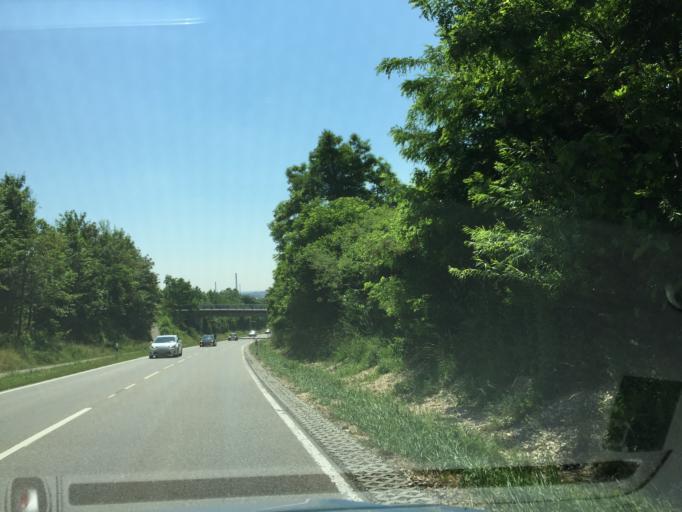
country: DE
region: Baden-Wuerttemberg
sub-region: Tuebingen Region
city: Ulm
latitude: 48.4107
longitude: 9.9438
